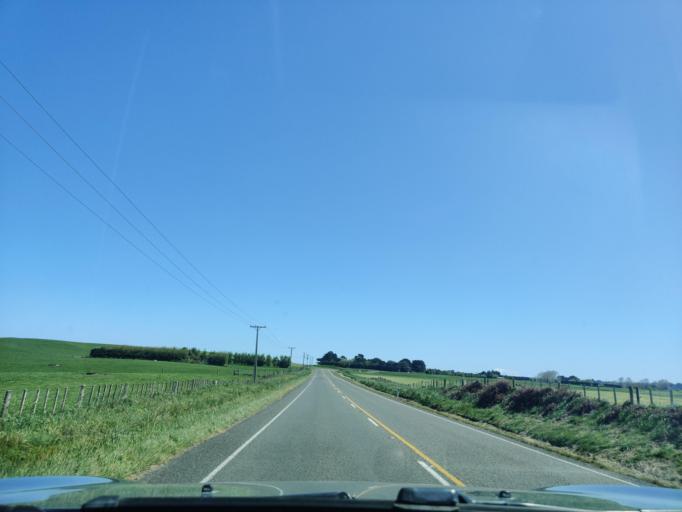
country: NZ
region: Taranaki
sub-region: South Taranaki District
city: Patea
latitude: -39.7972
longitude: 174.7121
